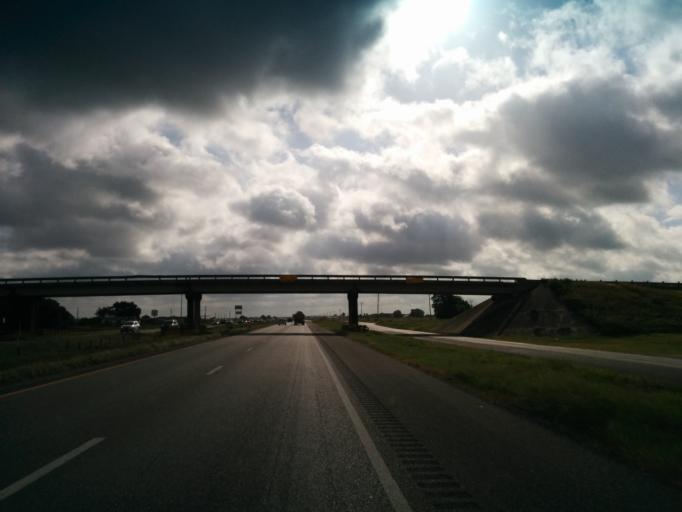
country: US
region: Texas
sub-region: Guadalupe County
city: Marion
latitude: 29.5186
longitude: -98.1396
